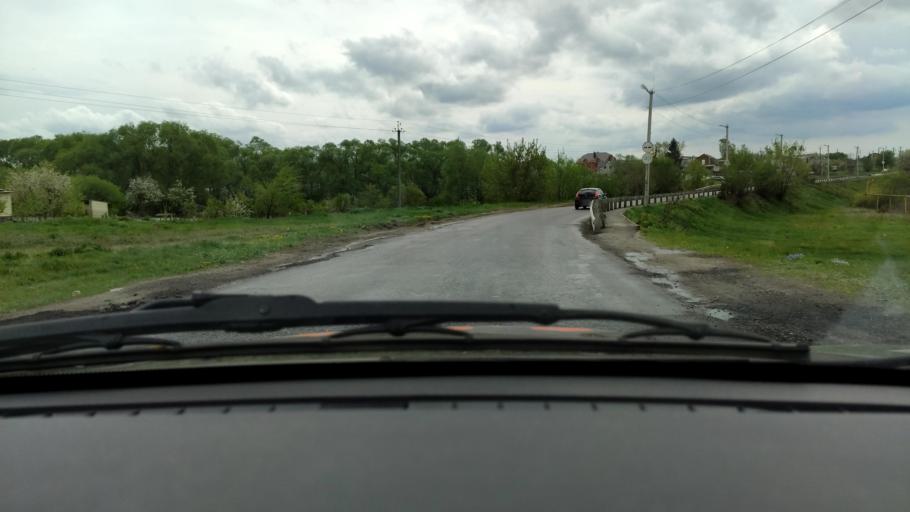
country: RU
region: Voronezj
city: Maslovka
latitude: 51.5394
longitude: 39.2342
